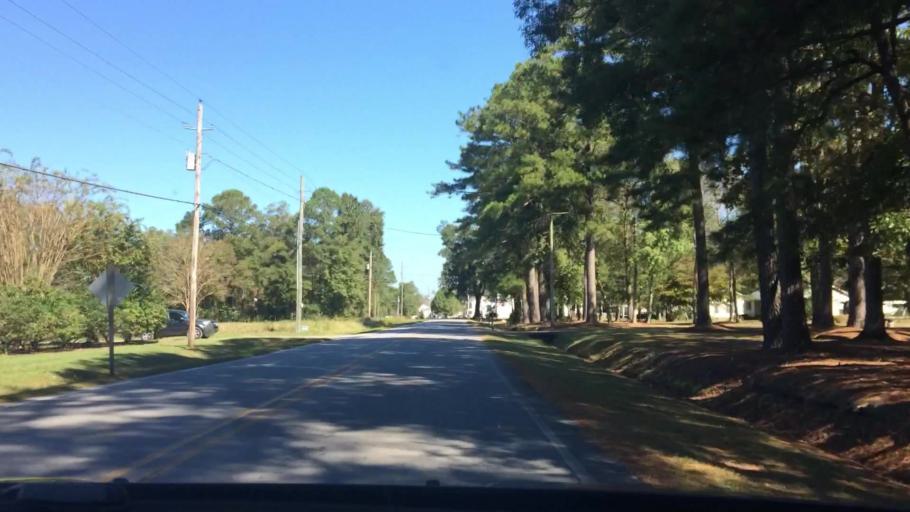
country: US
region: North Carolina
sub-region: Pitt County
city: Winterville
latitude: 35.5329
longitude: -77.4422
